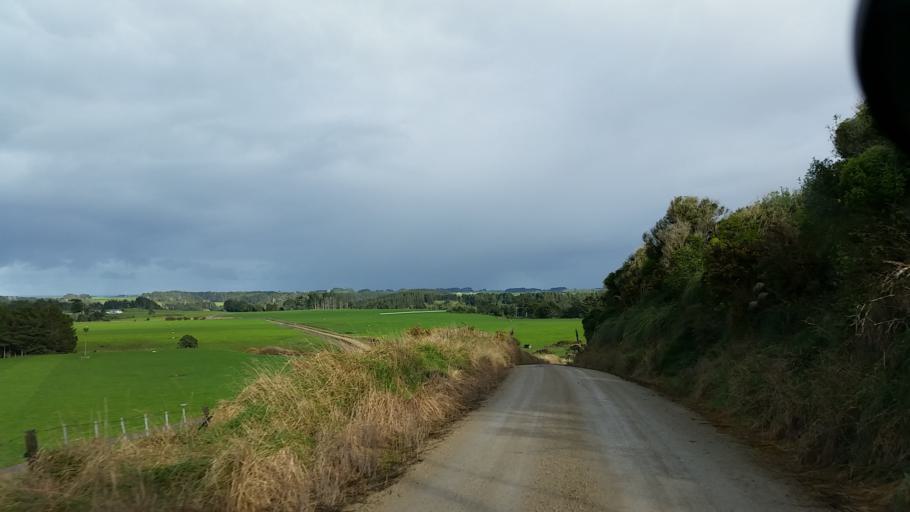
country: NZ
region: Taranaki
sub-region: South Taranaki District
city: Patea
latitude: -39.7298
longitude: 174.7093
